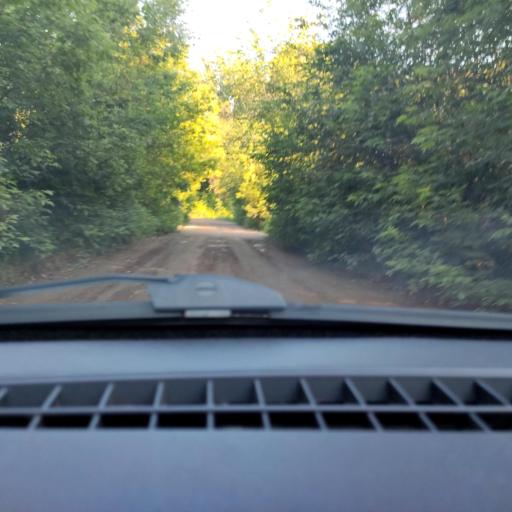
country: RU
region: Bashkortostan
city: Avdon
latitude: 54.6095
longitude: 55.6664
